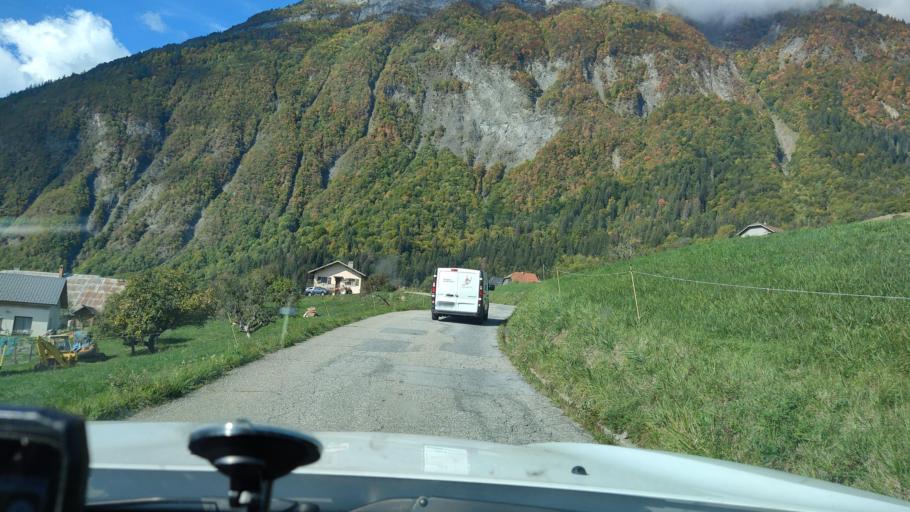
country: FR
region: Rhone-Alpes
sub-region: Departement de la Savoie
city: Ugine
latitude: 45.7678
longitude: 6.4025
